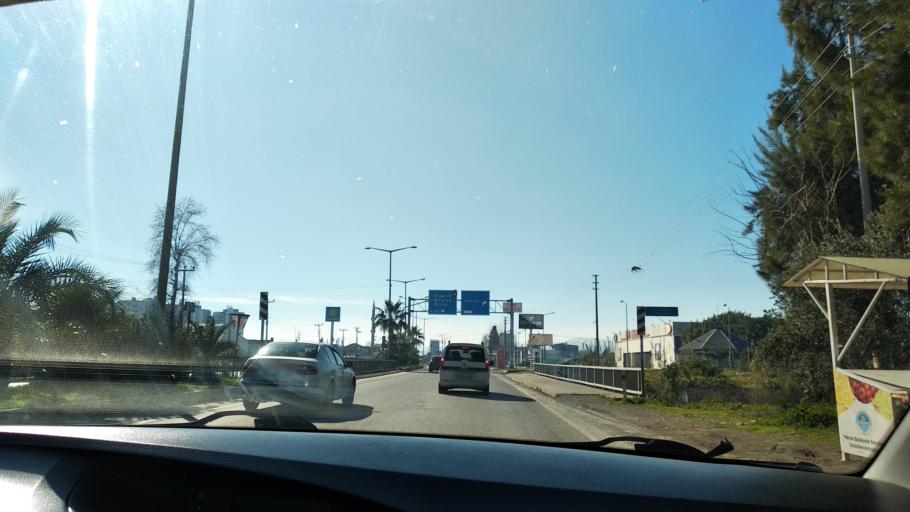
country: TR
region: Mersin
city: Tomuk
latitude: 36.6497
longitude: 34.3729
